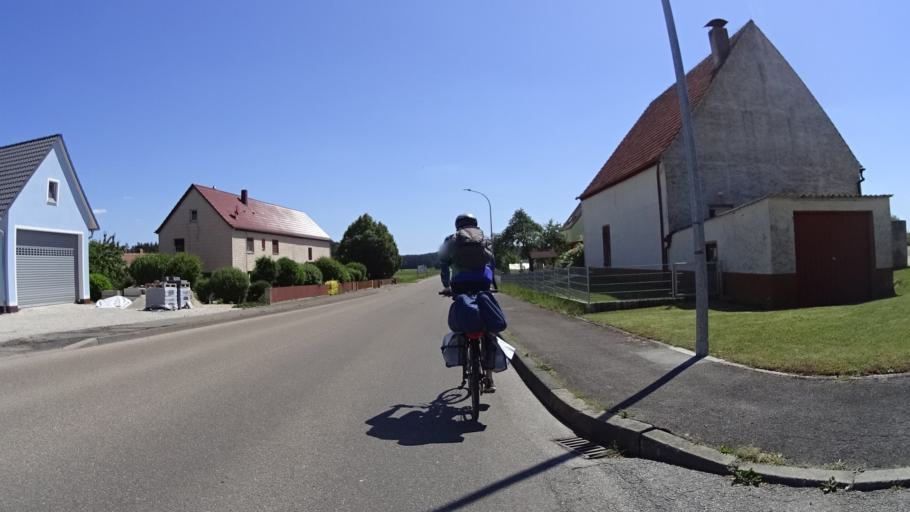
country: DE
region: Bavaria
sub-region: Regierungsbezirk Mittelfranken
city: Pfofeld
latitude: 49.1173
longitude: 10.8030
